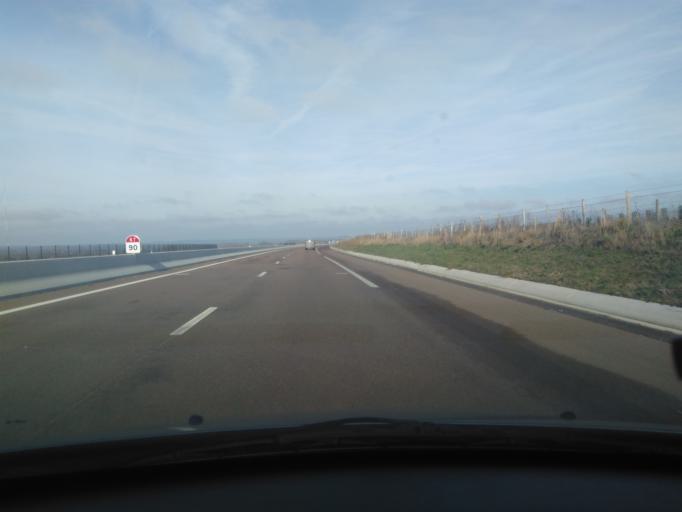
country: FR
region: Bourgogne
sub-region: Departement de la Nievre
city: Saint-Pierre-le-Moutier
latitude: 46.8208
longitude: 3.1247
